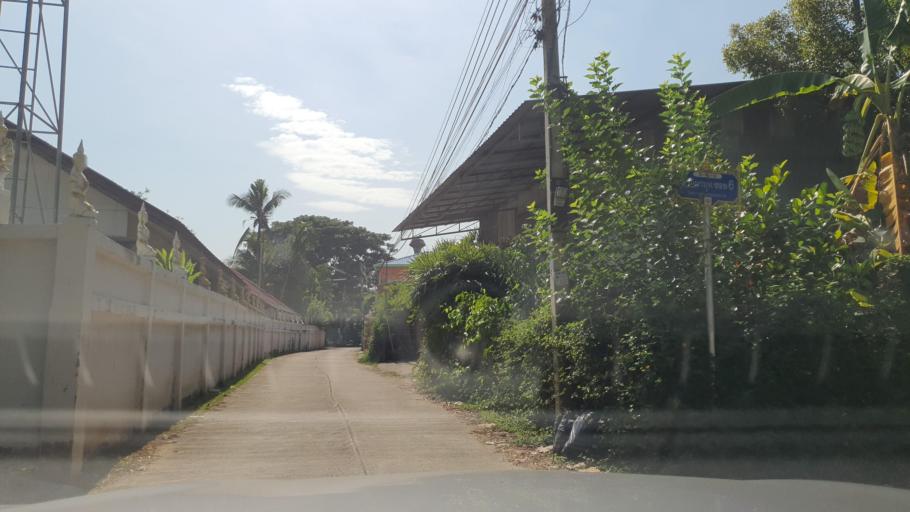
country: TH
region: Chiang Mai
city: Hang Dong
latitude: 18.7143
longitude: 98.9297
